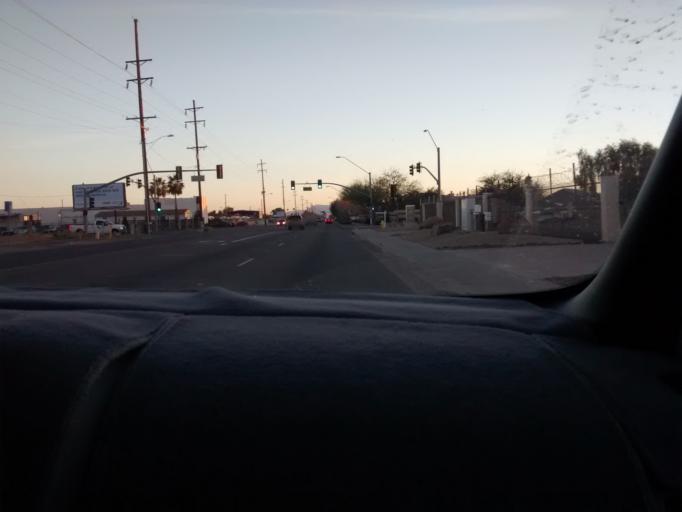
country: US
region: Arizona
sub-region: Maricopa County
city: Glendale
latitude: 33.5462
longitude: -112.2031
